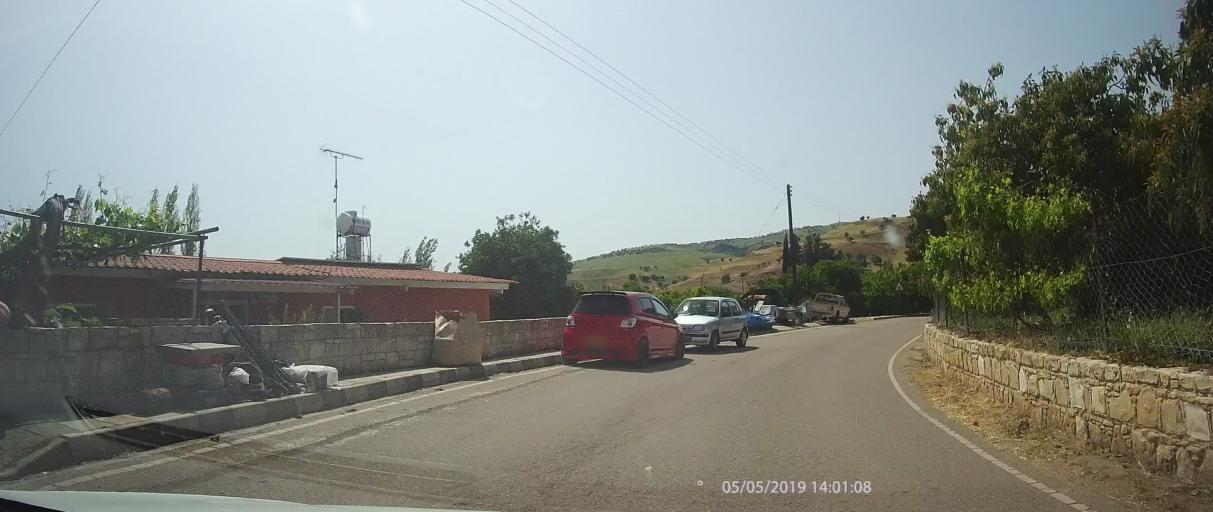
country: CY
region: Limassol
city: Pissouri
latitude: 34.7781
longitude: 32.6520
